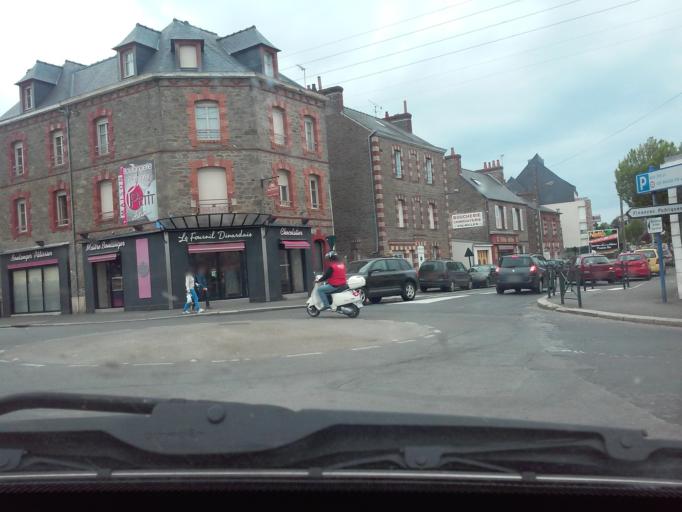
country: FR
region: Brittany
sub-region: Departement d'Ille-et-Vilaine
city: Dinard
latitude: 48.6306
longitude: -2.0637
